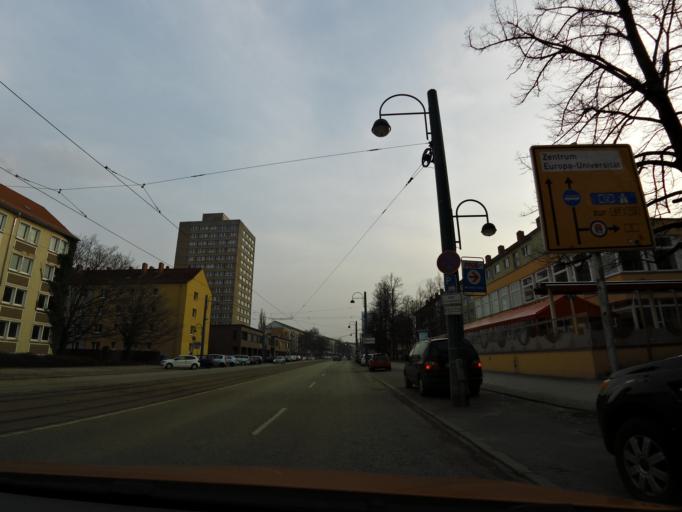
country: DE
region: Brandenburg
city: Frankfurt (Oder)
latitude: 52.3487
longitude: 14.5499
